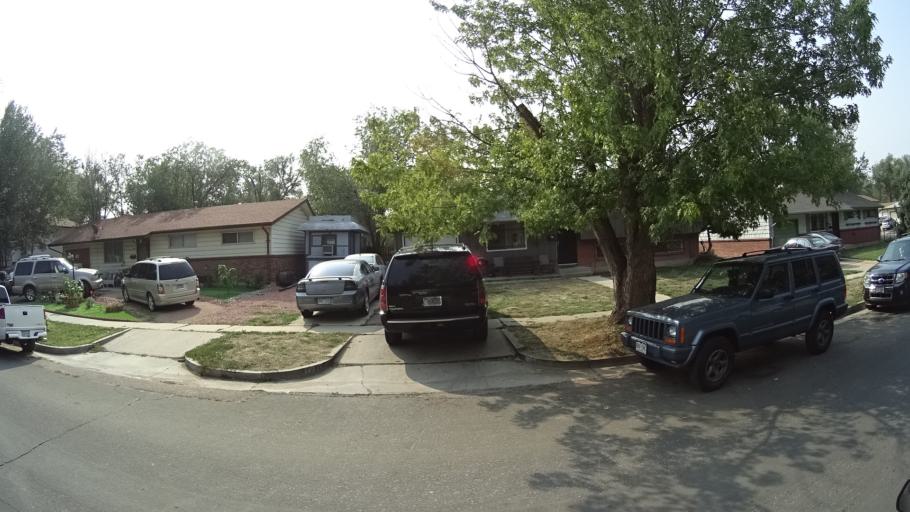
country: US
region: Colorado
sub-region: El Paso County
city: Stratmoor
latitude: 38.8146
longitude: -104.7786
